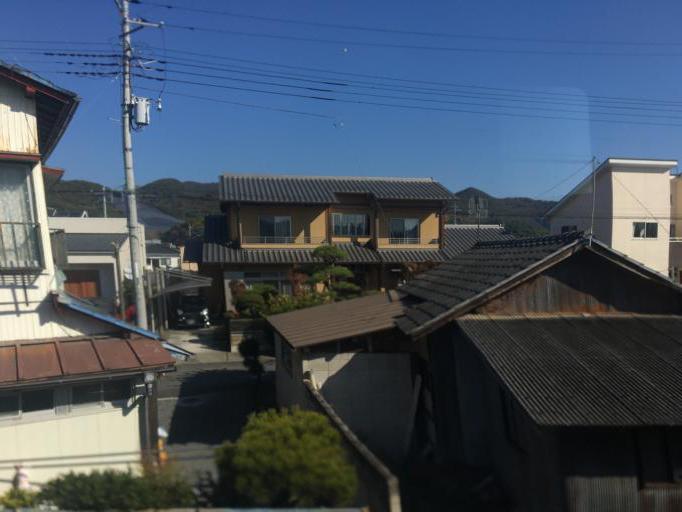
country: JP
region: Gunma
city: Kiryu
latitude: 36.3874
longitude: 139.3563
